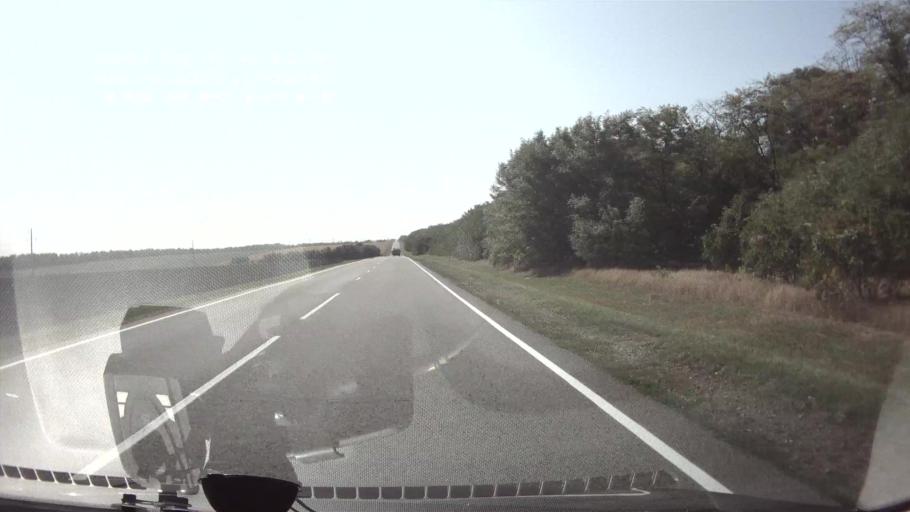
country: RU
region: Krasnodarskiy
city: Novopokrovskaya
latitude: 45.8524
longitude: 40.7210
